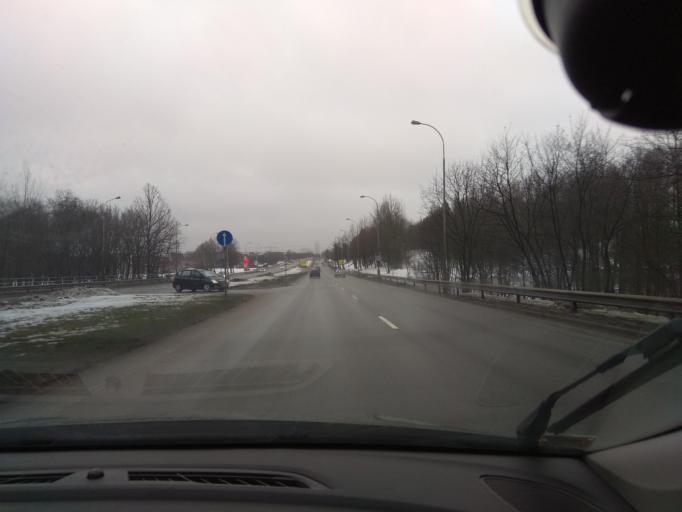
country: LT
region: Vilnius County
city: Seskine
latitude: 54.7246
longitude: 25.2692
